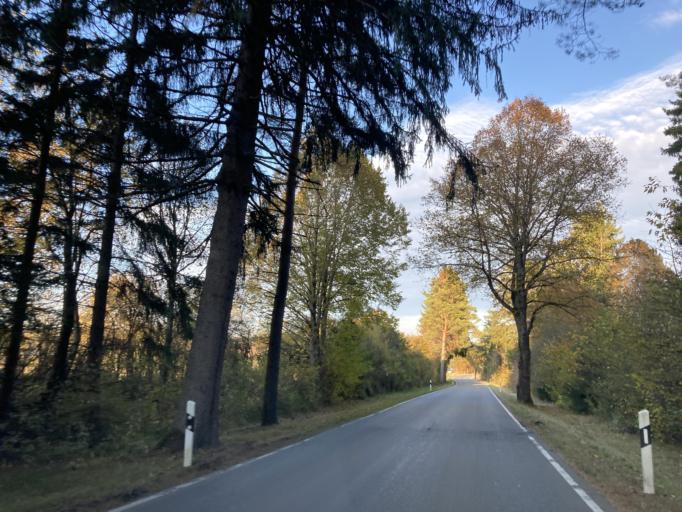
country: DE
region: Baden-Wuerttemberg
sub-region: Freiburg Region
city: Villingen-Schwenningen
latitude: 48.0075
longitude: 8.4416
